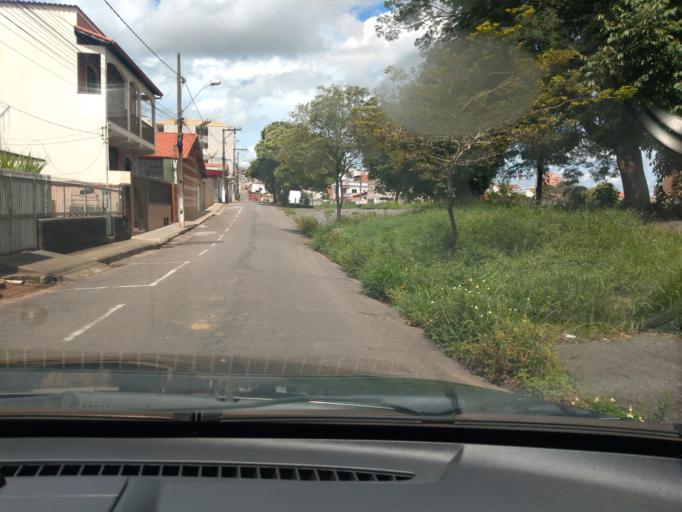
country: BR
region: Minas Gerais
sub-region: Tres Coracoes
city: Tres Coracoes
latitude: -21.6956
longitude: -45.2619
